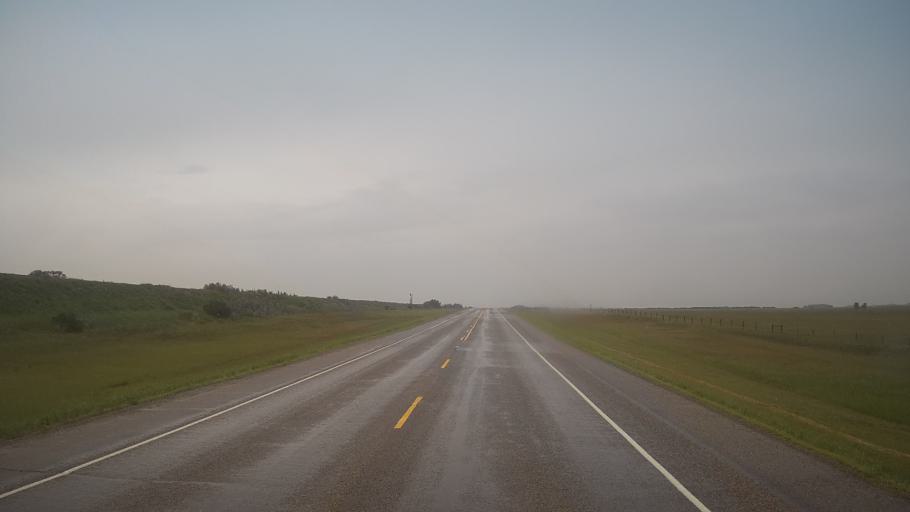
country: CA
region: Saskatchewan
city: Wilkie
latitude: 52.2157
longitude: -108.5033
